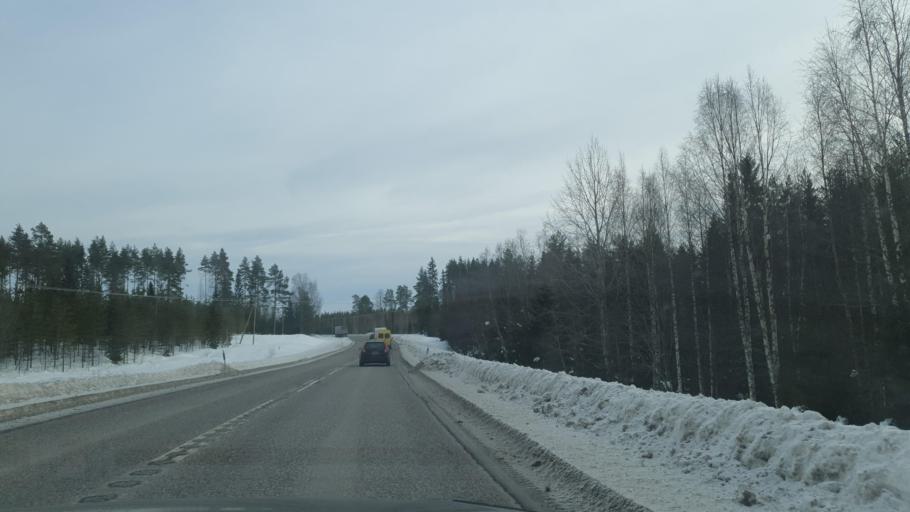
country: FI
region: Kainuu
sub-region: Kajaani
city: Kajaani
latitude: 64.4394
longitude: 27.5569
